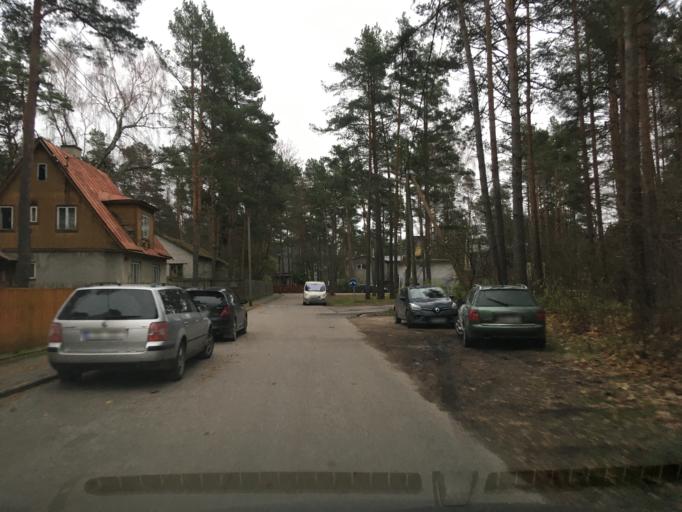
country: EE
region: Harju
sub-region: Saue vald
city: Laagri
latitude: 59.3801
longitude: 24.6900
